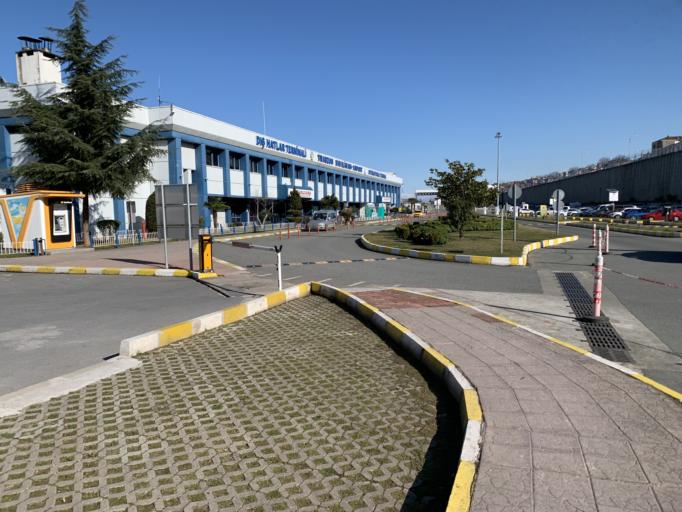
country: TR
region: Trabzon
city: Trabzon
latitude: 40.9942
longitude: 39.7810
